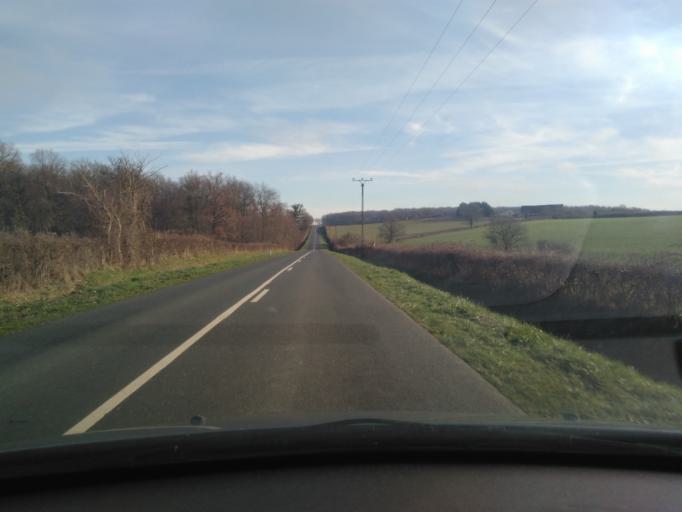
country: FR
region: Centre
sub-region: Departement de l'Indre
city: Montgivray
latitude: 46.6391
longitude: 2.0879
